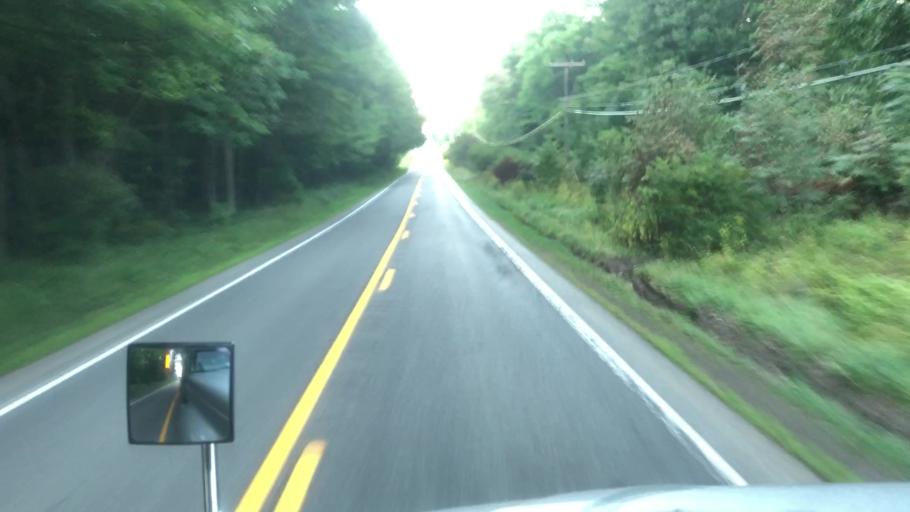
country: US
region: Pennsylvania
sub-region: Crawford County
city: Titusville
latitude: 41.5622
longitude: -79.6111
